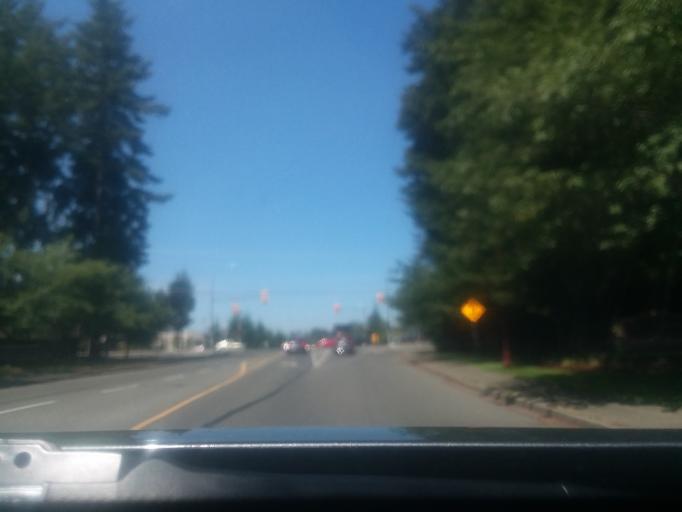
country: CA
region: British Columbia
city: Courtenay
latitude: 49.7121
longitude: -124.9604
